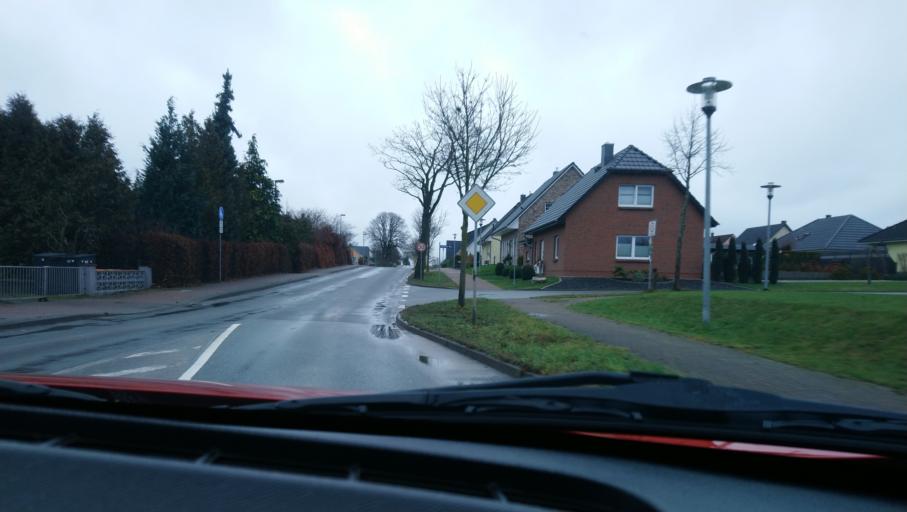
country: DE
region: Mecklenburg-Vorpommern
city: Seehof
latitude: 53.6835
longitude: 11.4294
